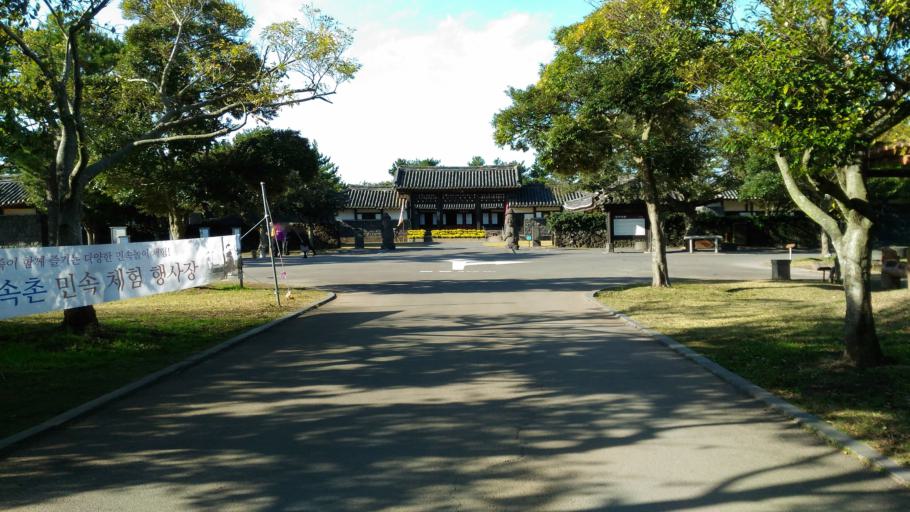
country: KR
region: Jeju-do
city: Seogwipo
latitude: 33.3218
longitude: 126.8427
